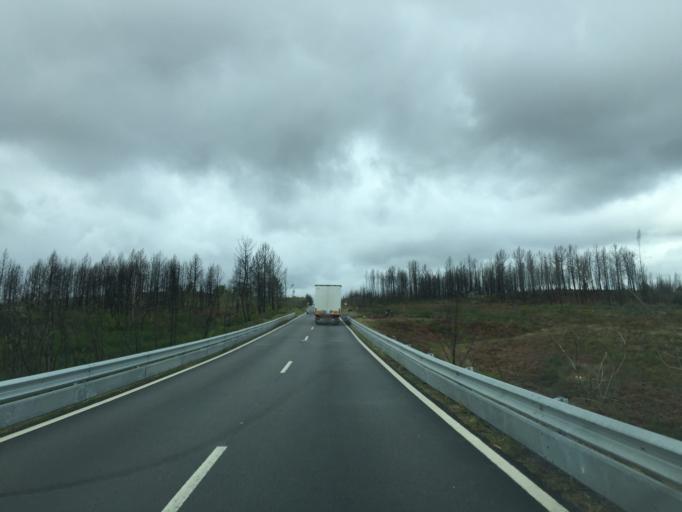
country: PT
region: Coimbra
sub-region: Oliveira do Hospital
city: Oliveira do Hospital
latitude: 40.3211
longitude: -7.9160
